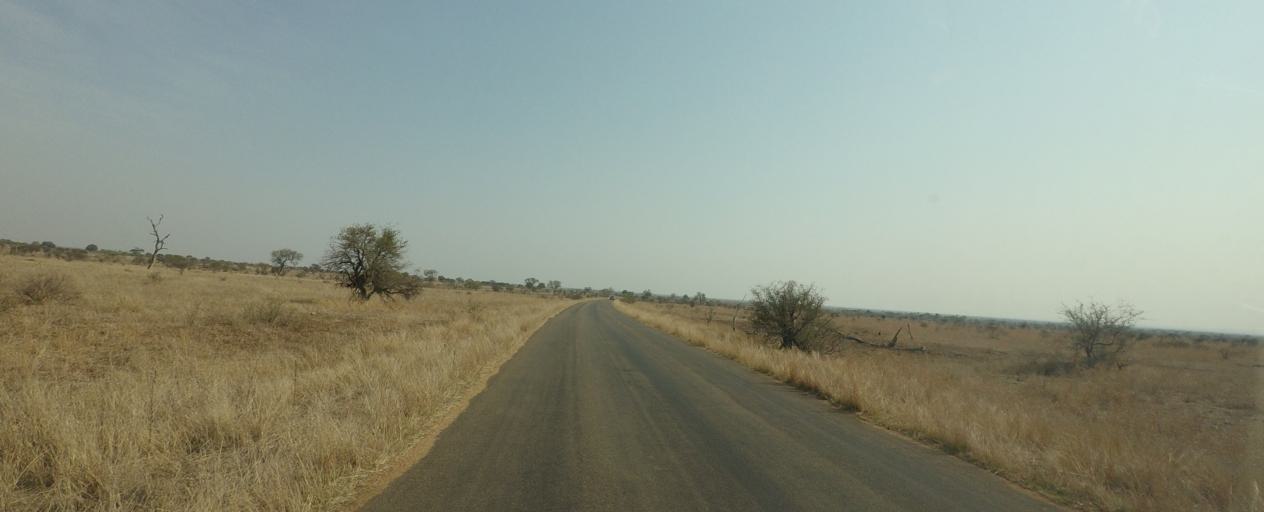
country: ZA
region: Limpopo
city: Thulamahashi
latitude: -24.3177
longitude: 31.7492
